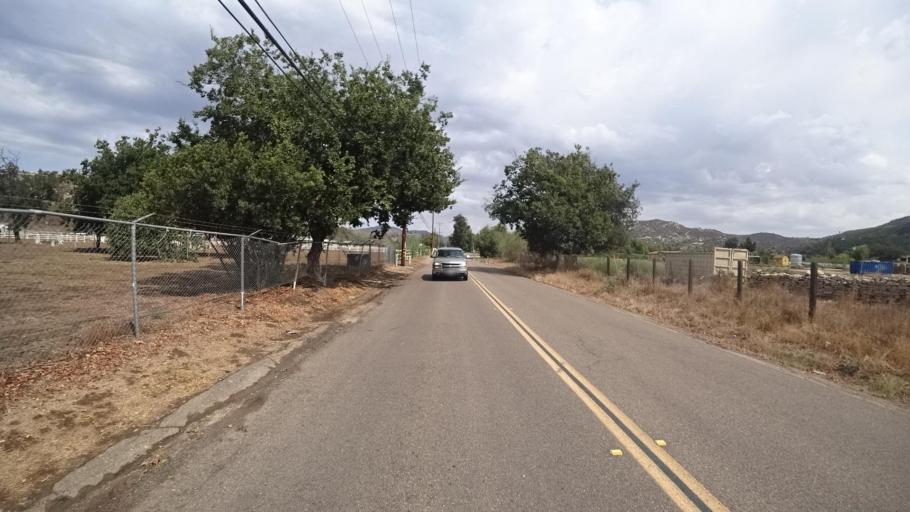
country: US
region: California
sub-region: San Diego County
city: Ramona
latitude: 33.0732
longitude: -116.8445
